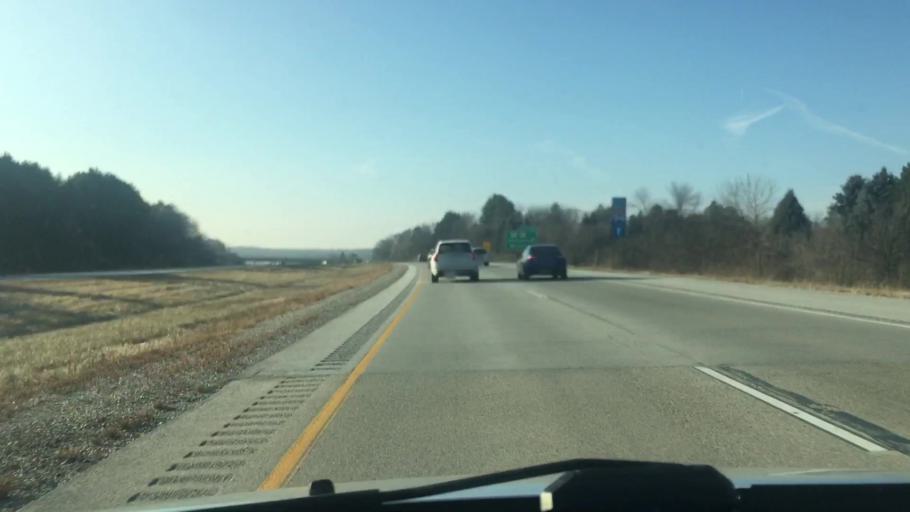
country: US
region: Wisconsin
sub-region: Waukesha County
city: Hartland
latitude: 43.1093
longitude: -88.3249
